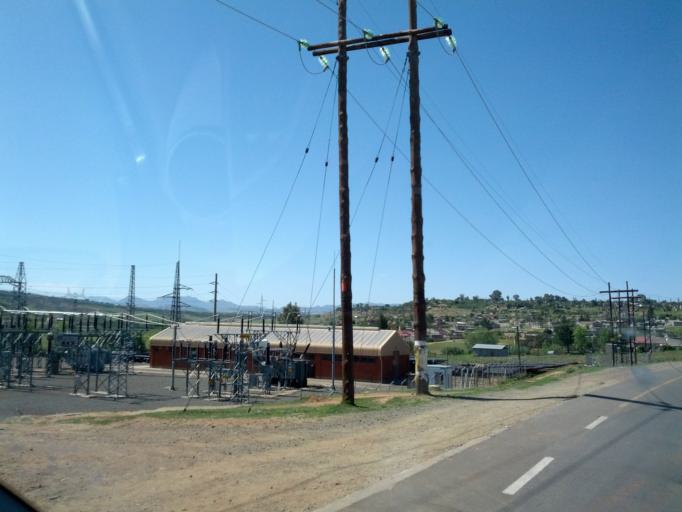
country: LS
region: Maseru
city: Maseru
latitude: -29.4057
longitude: 27.5622
